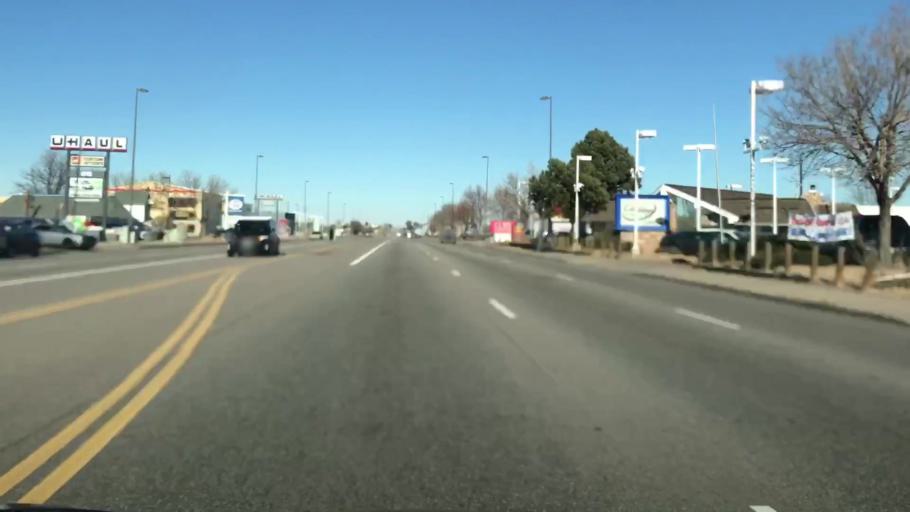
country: US
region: Colorado
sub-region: Adams County
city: Aurora
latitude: 39.7043
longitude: -104.8660
